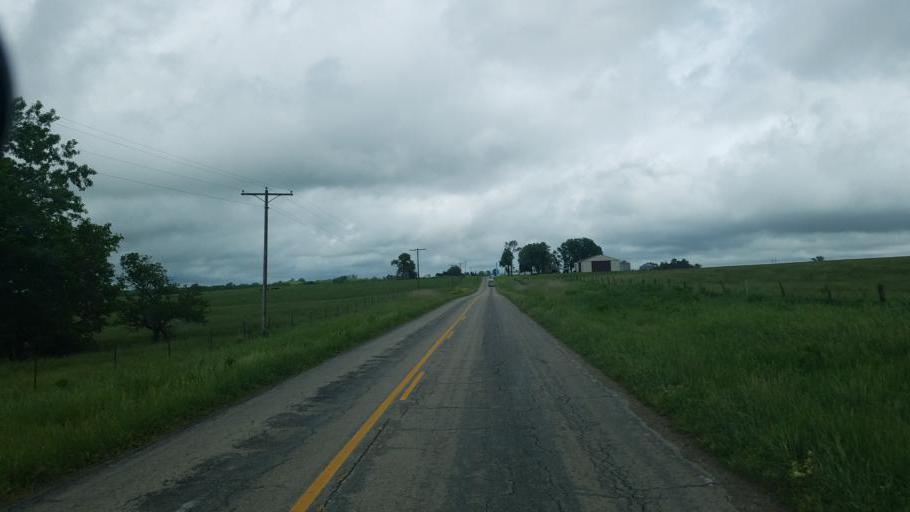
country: US
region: Missouri
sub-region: Mercer County
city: Princeton
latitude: 40.3626
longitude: -93.6806
